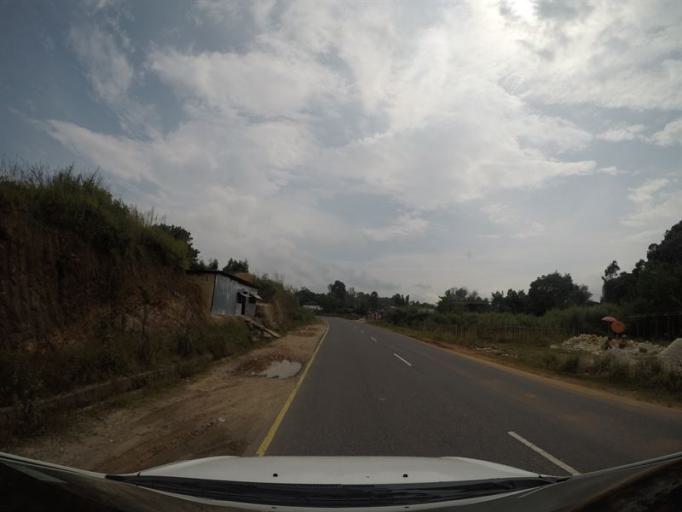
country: IN
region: Meghalaya
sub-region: East Khasi Hills
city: Shillong
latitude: 25.4859
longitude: 92.1919
